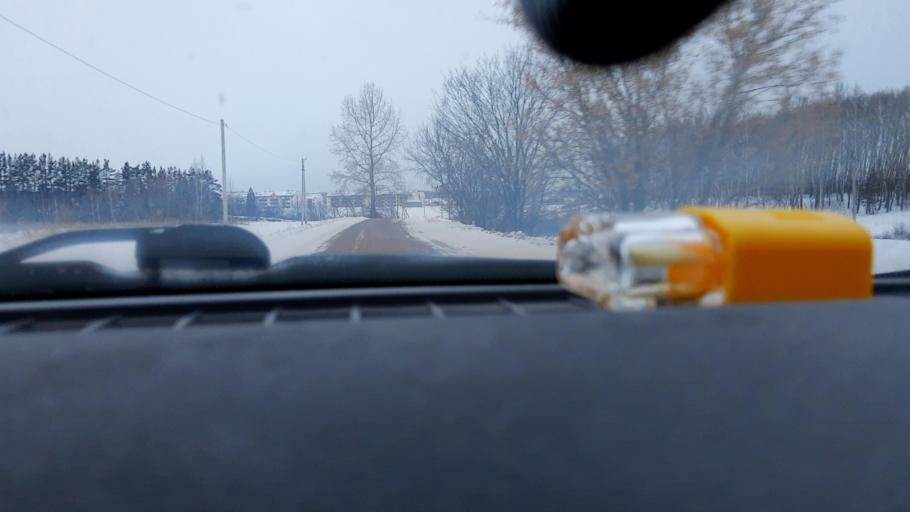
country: RU
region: Bashkortostan
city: Iglino
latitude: 54.8048
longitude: 56.4202
